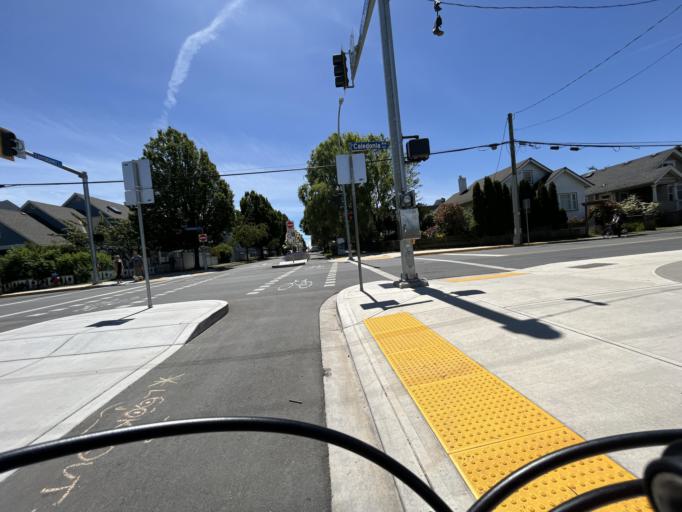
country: CA
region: British Columbia
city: Victoria
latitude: 48.4307
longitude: -123.3558
